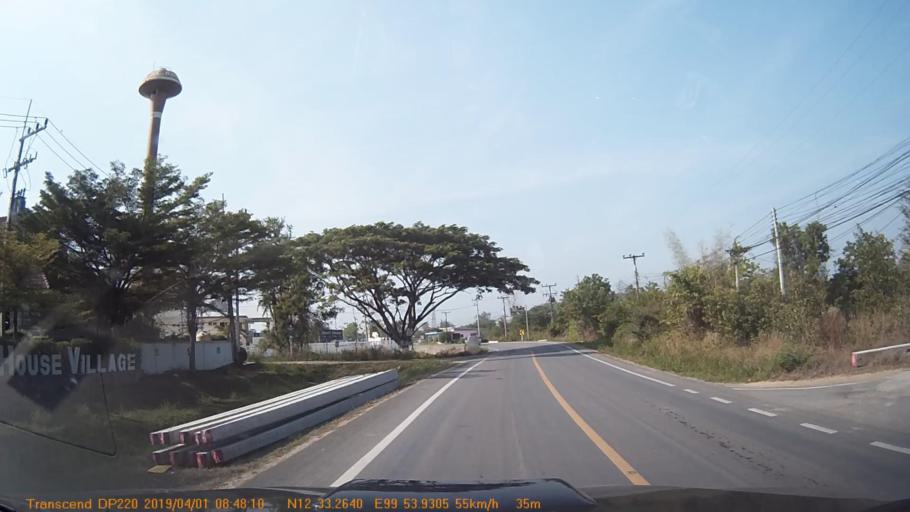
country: TH
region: Prachuap Khiri Khan
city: Hua Hin
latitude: 12.5541
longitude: 99.8988
